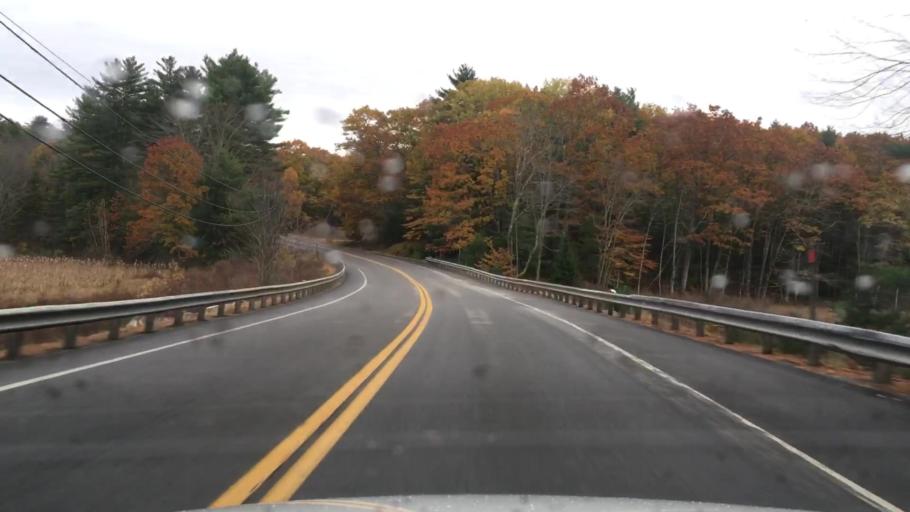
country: US
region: Maine
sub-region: Lincoln County
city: Jefferson
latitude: 44.2043
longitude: -69.5023
